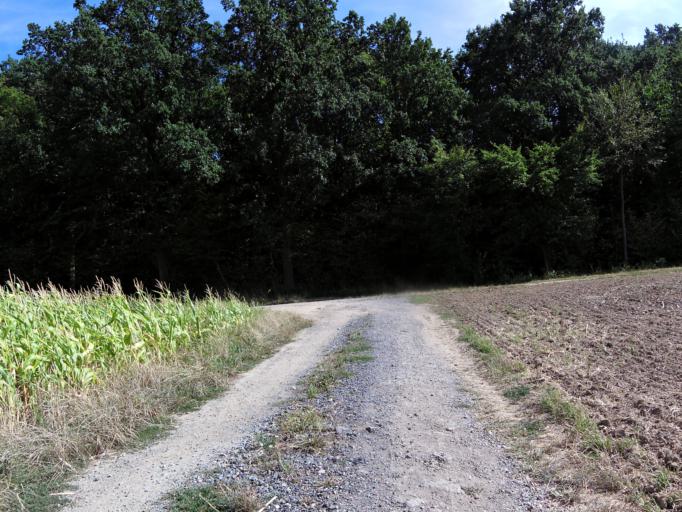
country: DE
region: Bavaria
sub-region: Regierungsbezirk Unterfranken
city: Theilheim
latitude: 49.7481
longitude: 10.0295
